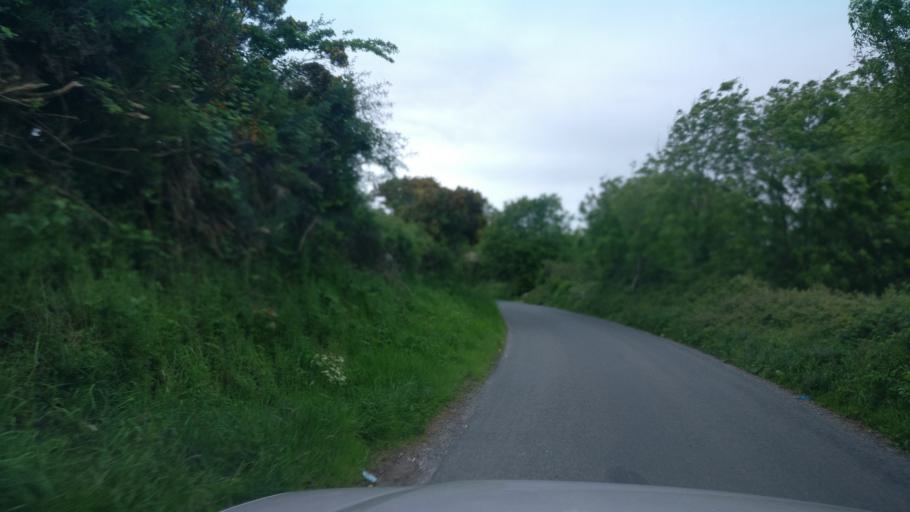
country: IE
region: Connaught
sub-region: County Galway
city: Loughrea
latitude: 53.1228
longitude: -8.4418
